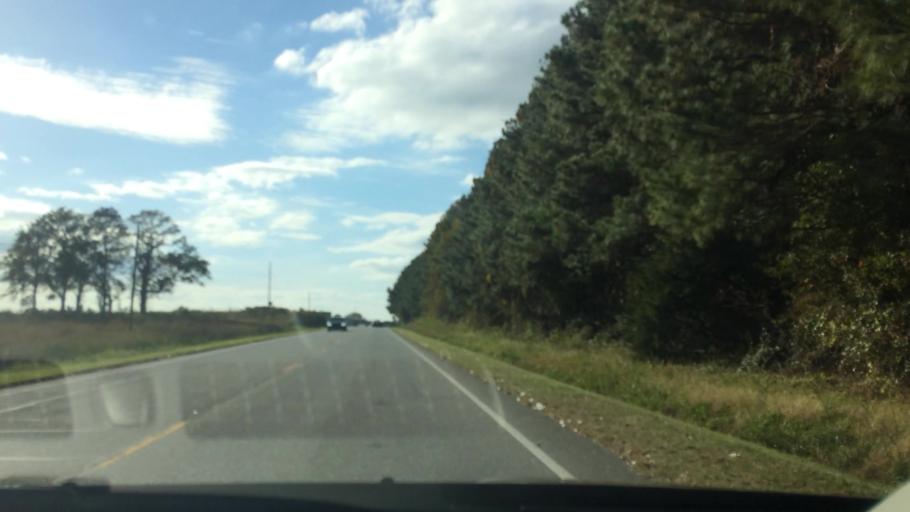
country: US
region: North Carolina
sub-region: Wayne County
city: Elroy
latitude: 35.4415
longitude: -77.8197
